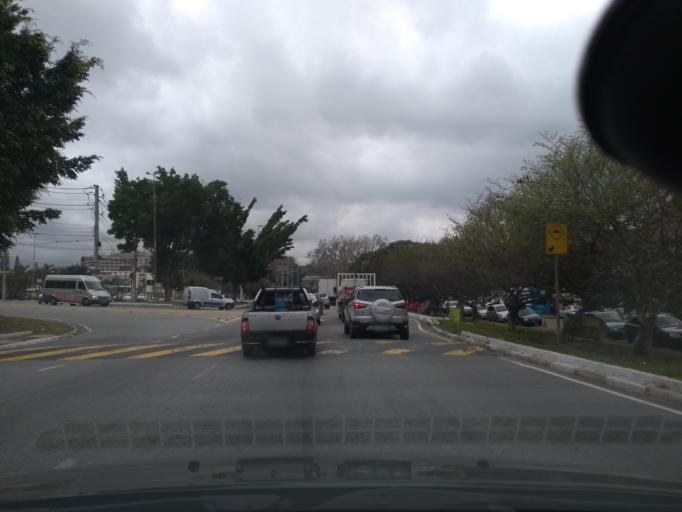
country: BR
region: Sao Paulo
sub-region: Guarulhos
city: Guarulhos
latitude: -23.4594
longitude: -46.4960
